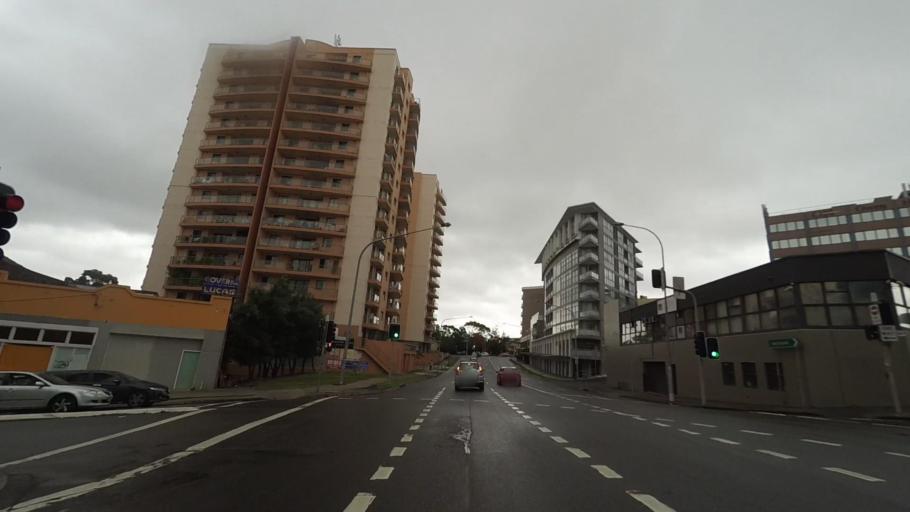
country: AU
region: New South Wales
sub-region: Kogarah
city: Hurstville Grove
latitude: -33.9688
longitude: 151.1038
